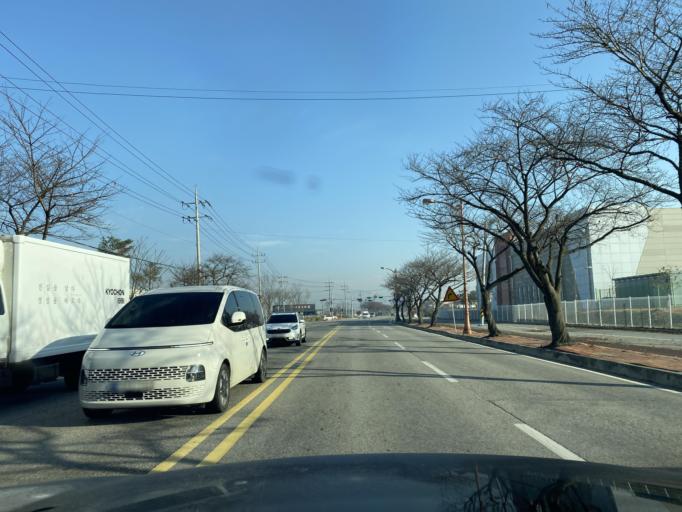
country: KR
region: Chungcheongnam-do
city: Yesan
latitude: 36.7168
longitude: 126.8439
